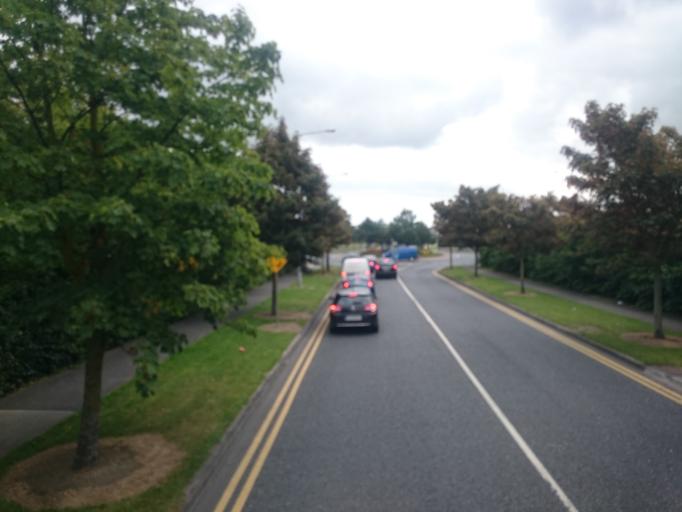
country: IE
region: Leinster
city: Tallaght
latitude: 53.2905
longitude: -6.3694
